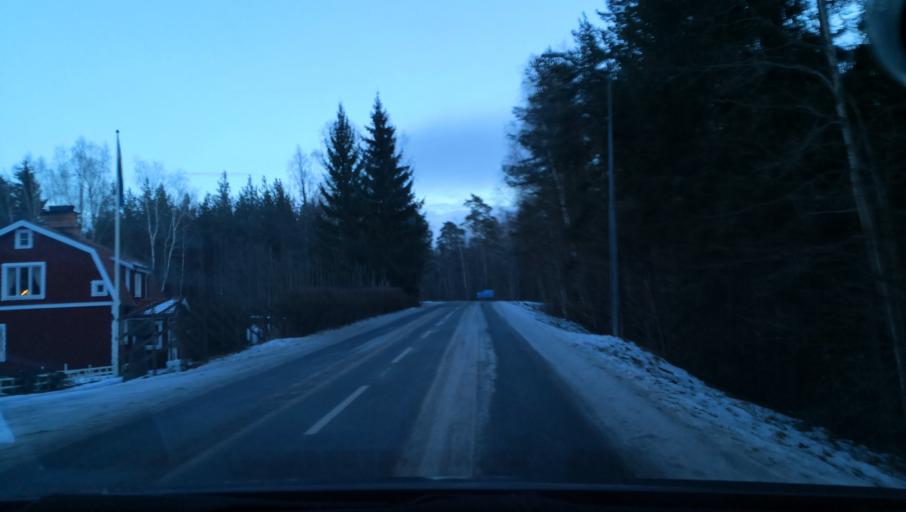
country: SE
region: Soedermanland
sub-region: Katrineholms Kommun
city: Katrineholm
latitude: 59.0840
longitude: 16.2210
